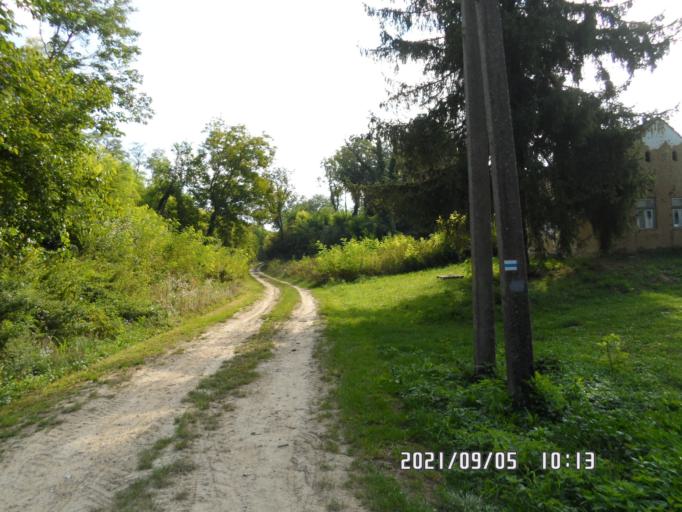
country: HU
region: Somogy
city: Bohonye
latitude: 46.4963
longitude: 17.3237
